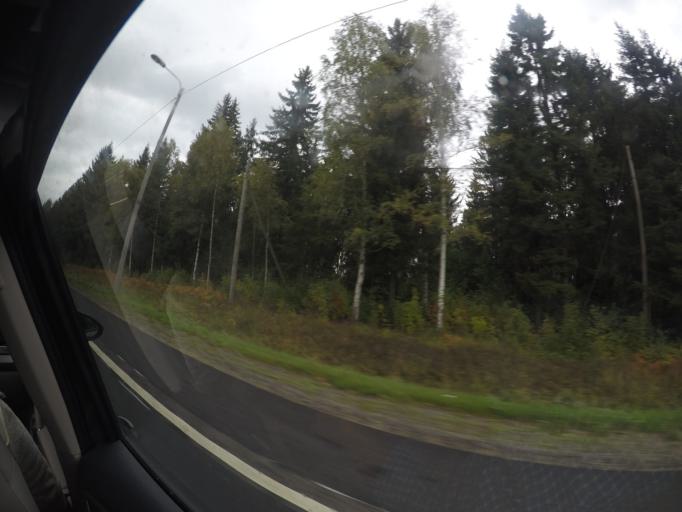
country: FI
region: Pirkanmaa
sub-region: Tampere
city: Kangasala
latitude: 61.4425
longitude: 24.1177
